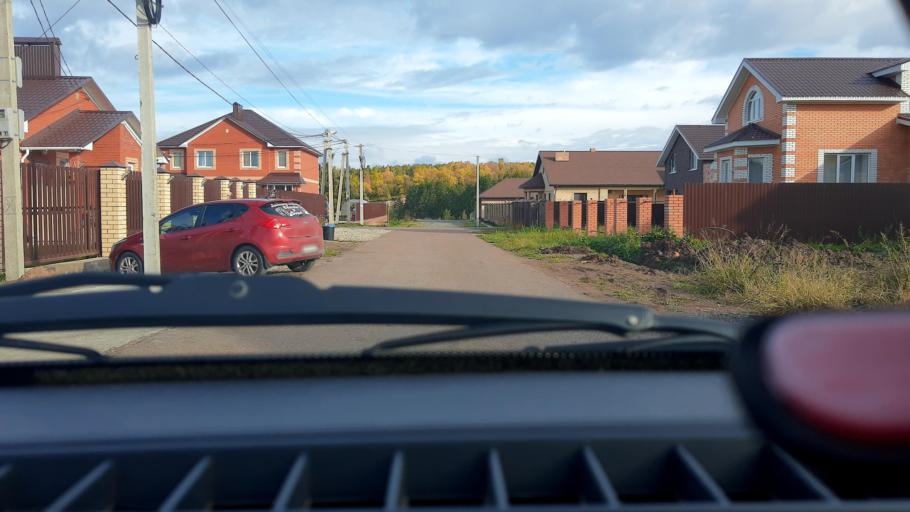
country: RU
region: Bashkortostan
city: Kabakovo
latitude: 54.6572
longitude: 56.1894
